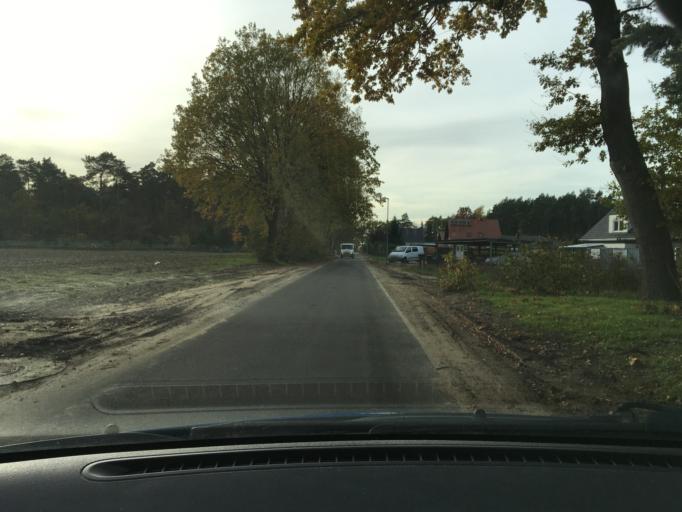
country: DE
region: Lower Saxony
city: Wittorf
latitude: 53.3224
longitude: 10.3631
